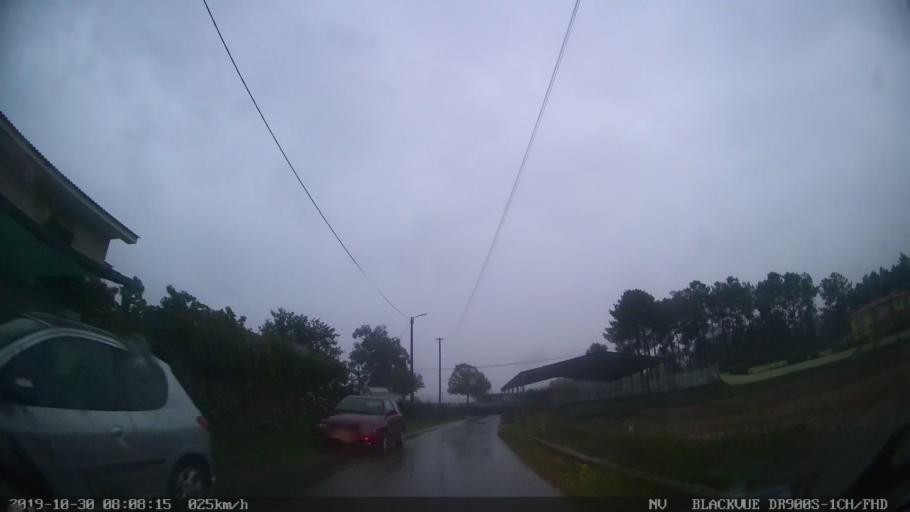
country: PT
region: Vila Real
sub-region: Vila Real
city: Vila Real
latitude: 41.3144
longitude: -7.7715
